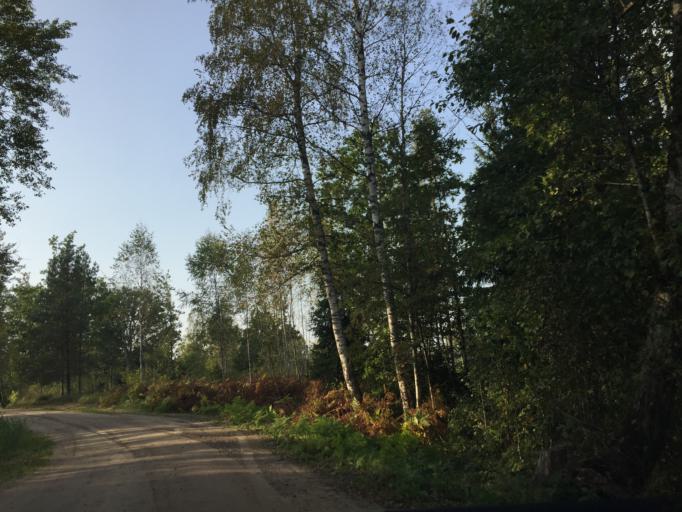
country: LV
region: Garkalne
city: Garkalne
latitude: 56.9728
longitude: 24.4217
